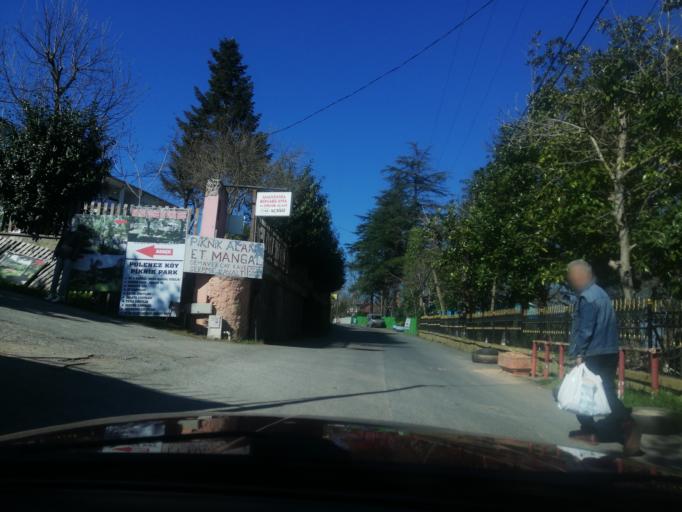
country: TR
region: Istanbul
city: Mahmut Sevket Pasa
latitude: 41.1123
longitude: 29.2112
